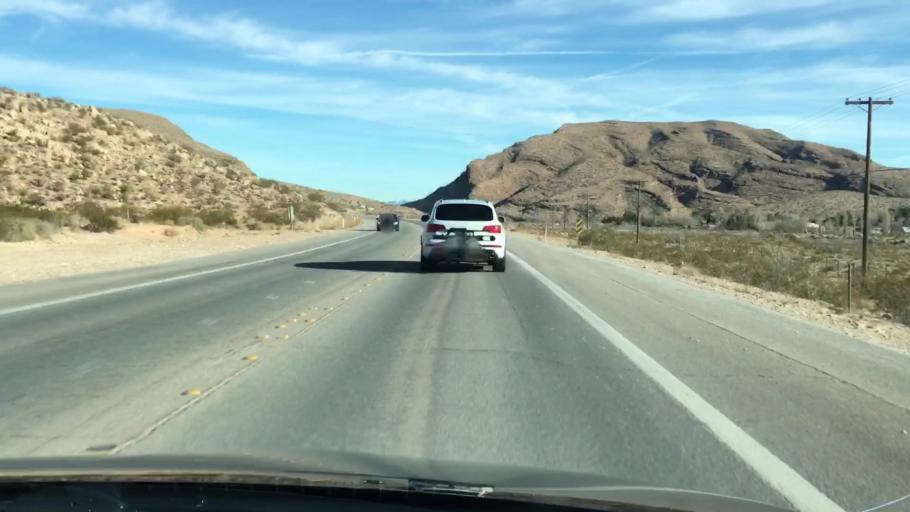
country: US
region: Nevada
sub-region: Clark County
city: Summerlin South
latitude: 36.0522
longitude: -115.4111
